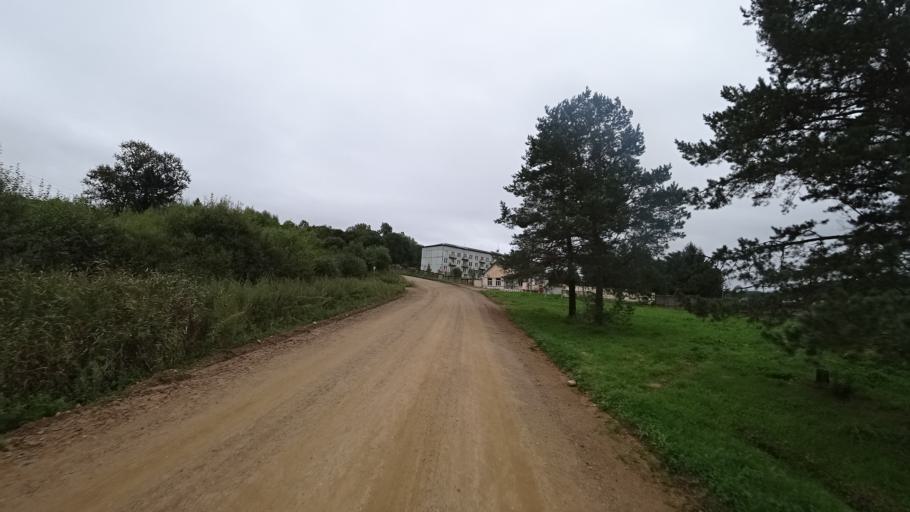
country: RU
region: Primorskiy
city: Rettikhovka
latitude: 44.1728
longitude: 132.8788
